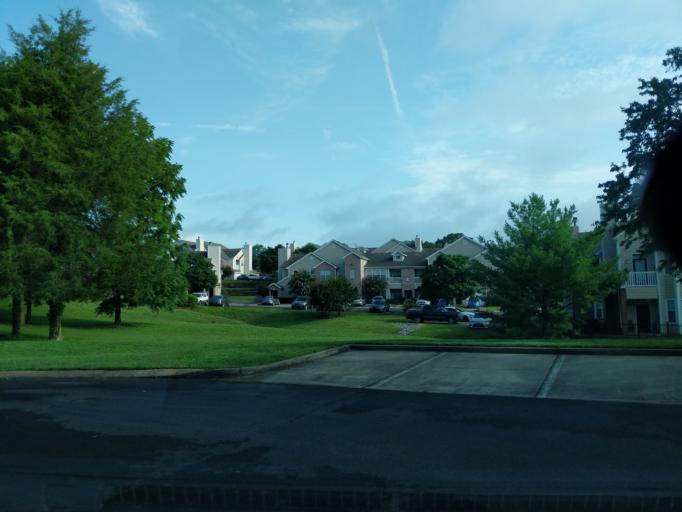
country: US
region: Tennessee
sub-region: Davidson County
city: Goodlettsville
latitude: 36.3036
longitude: -86.6780
